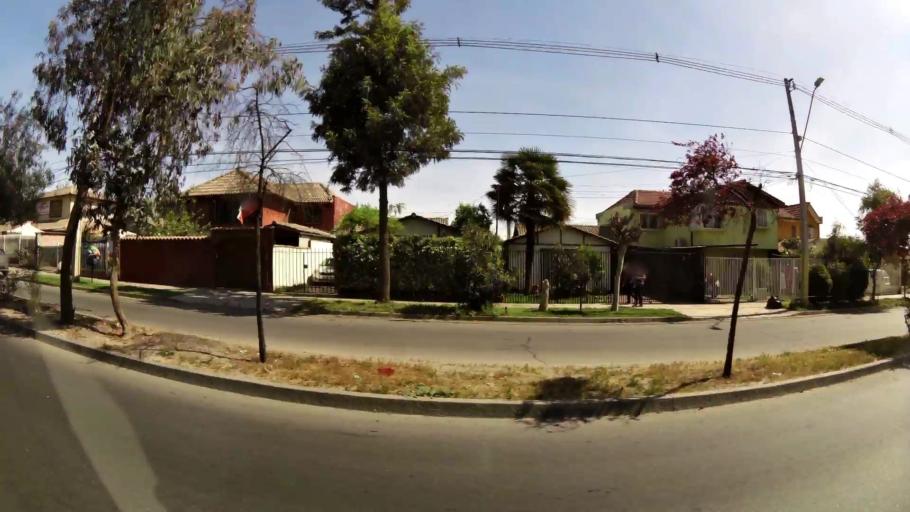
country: CL
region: Santiago Metropolitan
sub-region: Provincia de Cordillera
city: Puente Alto
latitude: -33.5780
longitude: -70.5525
